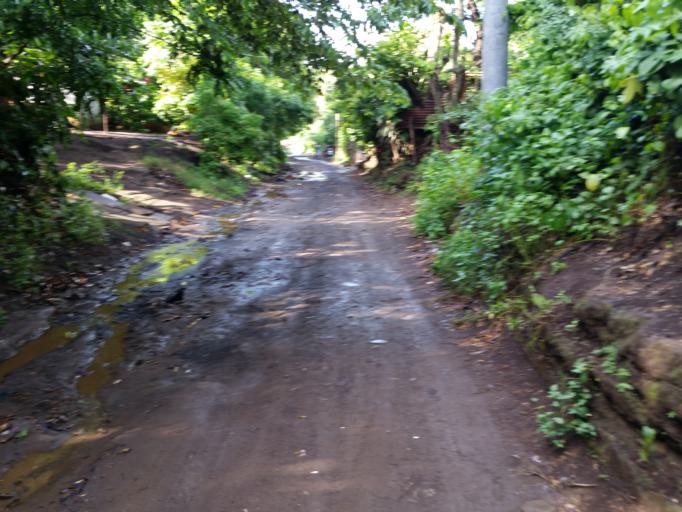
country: NI
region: Managua
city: Managua
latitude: 12.0877
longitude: -86.2561
